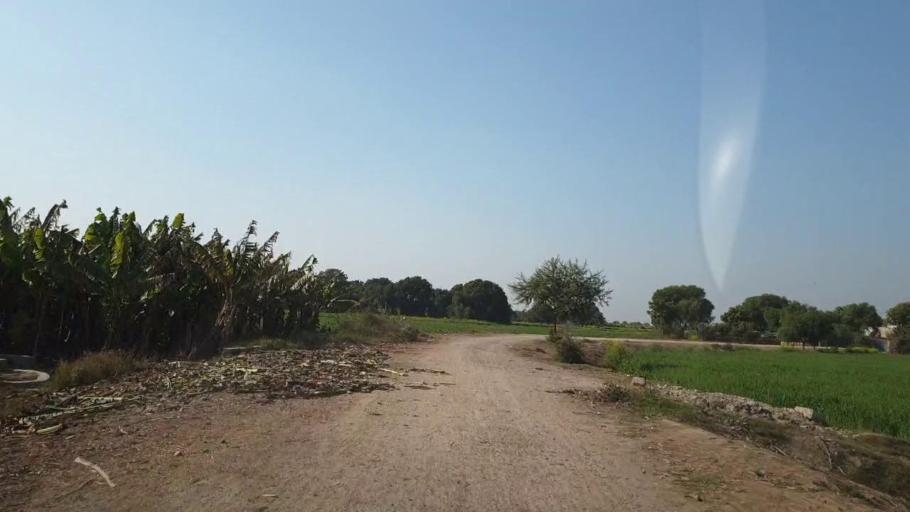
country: PK
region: Sindh
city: Tando Jam
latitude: 25.5072
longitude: 68.5377
